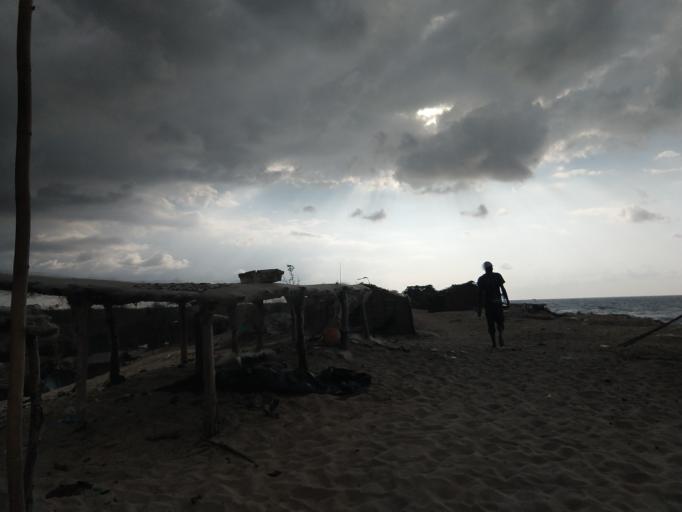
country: MZ
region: Sofala
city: Beira
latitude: -19.6772
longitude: 35.1476
